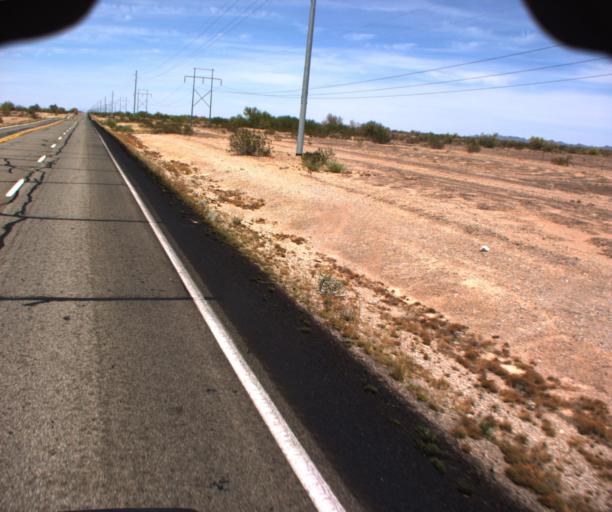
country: US
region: Arizona
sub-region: La Paz County
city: Quartzsite
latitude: 33.7736
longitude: -114.2170
